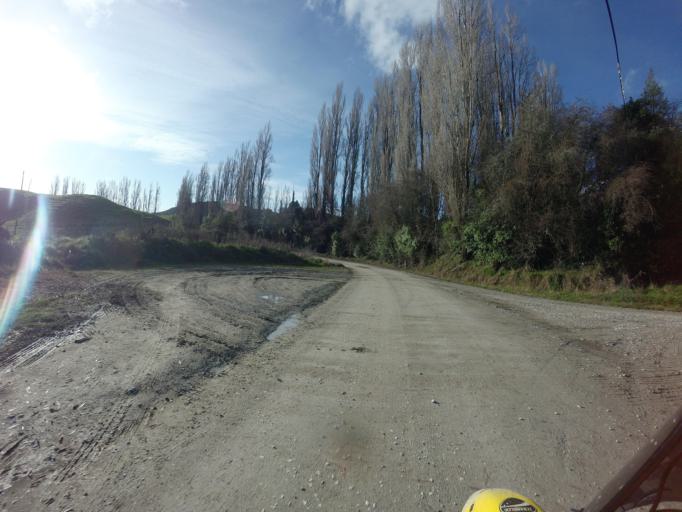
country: NZ
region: Hawke's Bay
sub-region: Wairoa District
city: Wairoa
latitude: -38.7668
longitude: 177.5658
